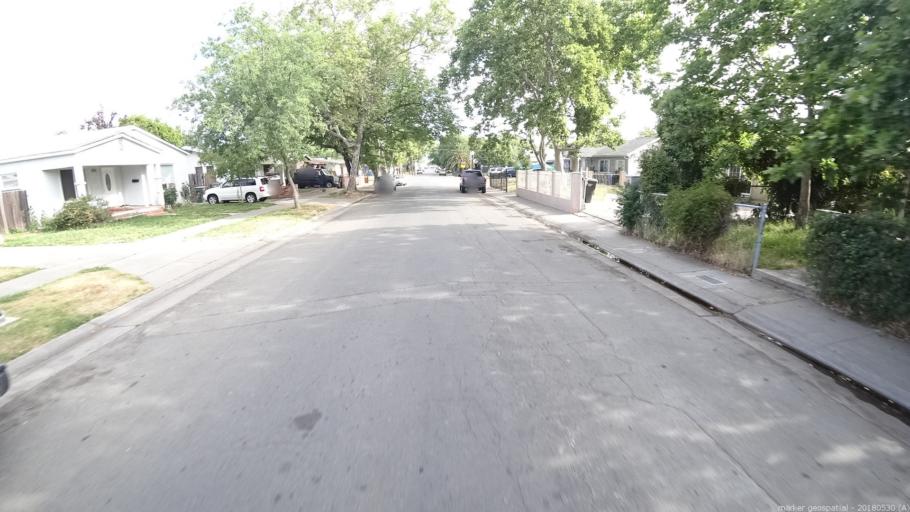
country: US
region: California
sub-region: Sacramento County
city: Sacramento
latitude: 38.6086
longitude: -121.4486
